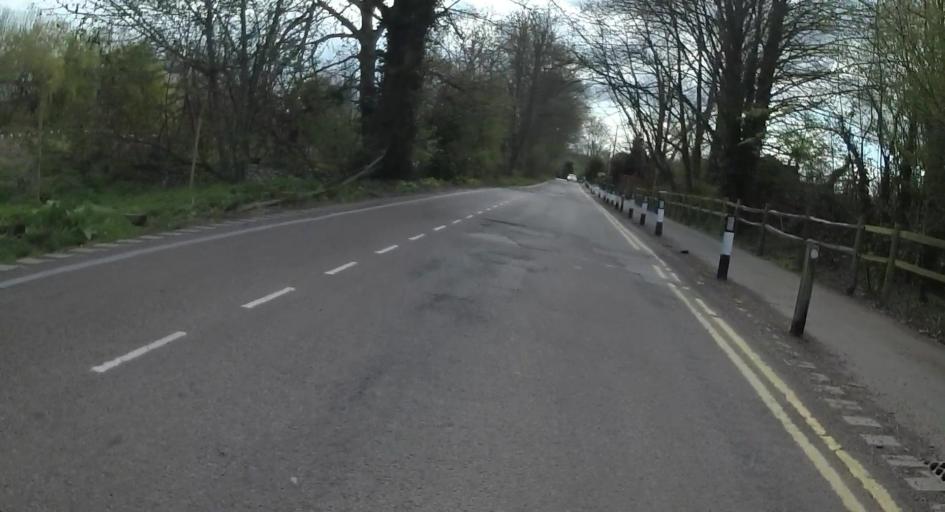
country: GB
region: England
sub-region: Surrey
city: Shepperton
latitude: 51.3860
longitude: -0.4582
